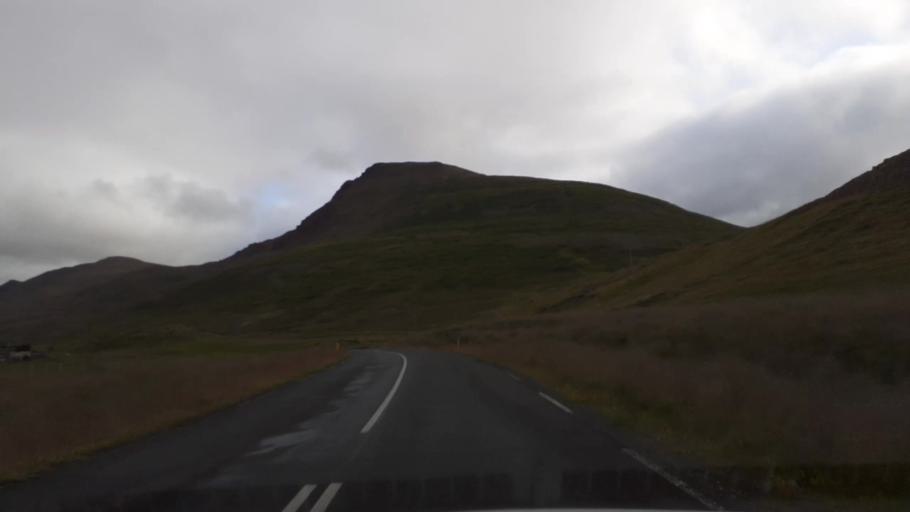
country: IS
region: Northeast
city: Akureyri
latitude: 65.8140
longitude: -18.0497
